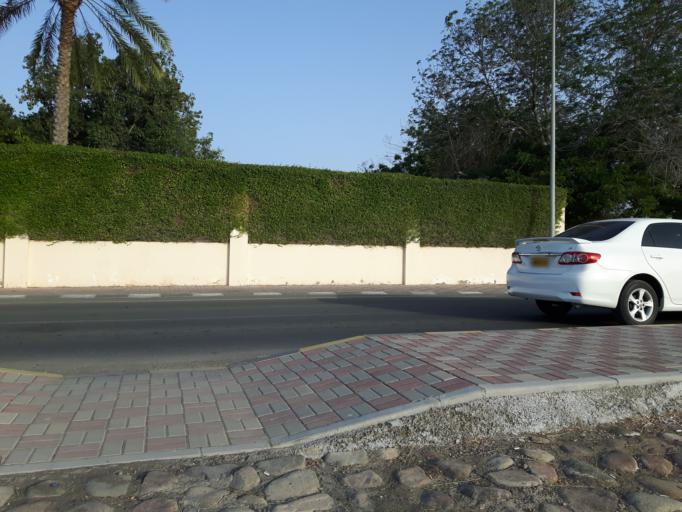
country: OM
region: Al Batinah
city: Al Sohar
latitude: 24.4023
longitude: 56.7117
